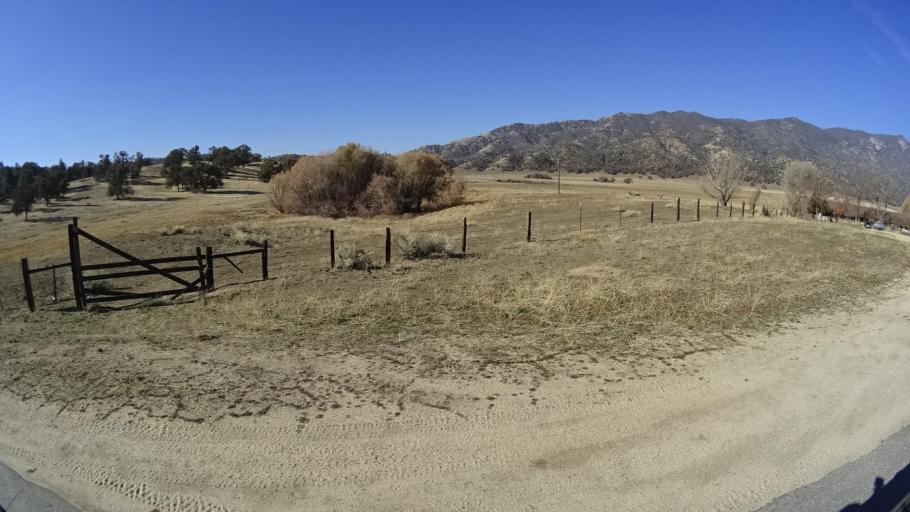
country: US
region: California
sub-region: Kern County
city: Bodfish
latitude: 35.3879
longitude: -118.5347
